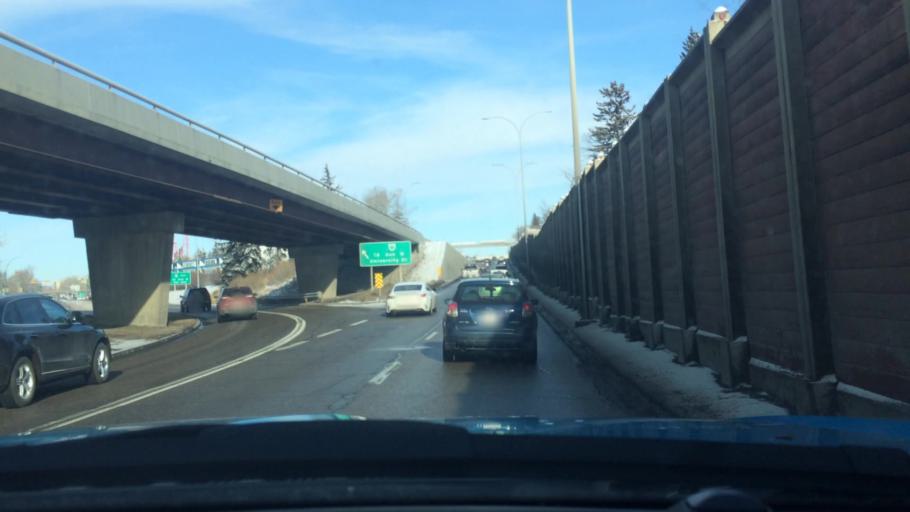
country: CA
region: Alberta
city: Calgary
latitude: 51.0622
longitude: -114.1178
